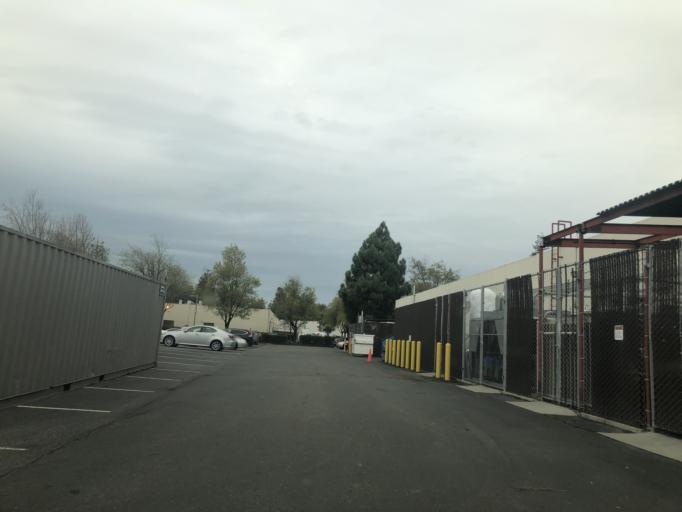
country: US
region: California
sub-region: Santa Clara County
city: San Jose
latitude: 37.3787
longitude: -121.9164
